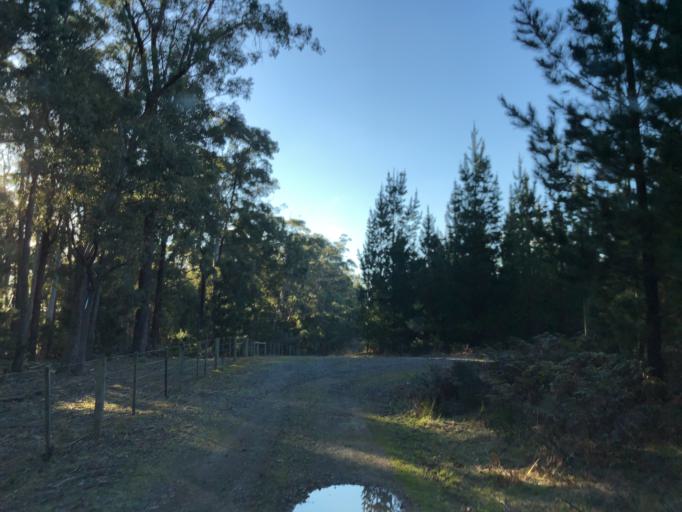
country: AU
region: Victoria
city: Brown Hill
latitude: -37.4982
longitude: 144.1455
